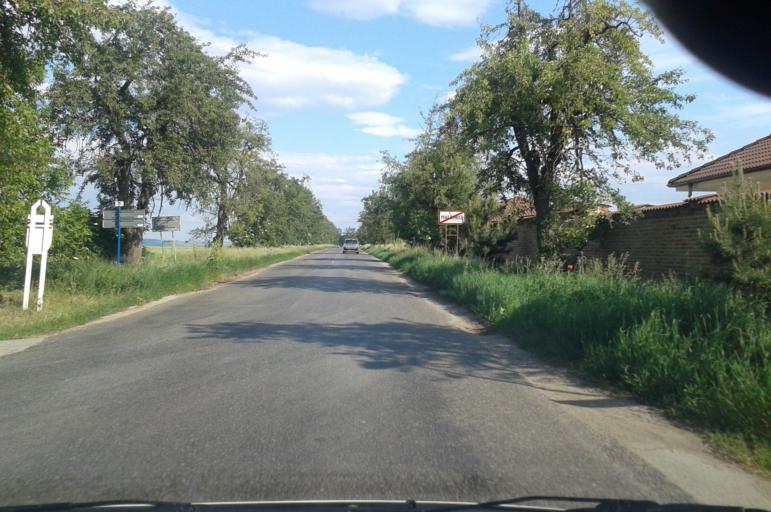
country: SK
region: Trnavsky
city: Leopoldov
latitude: 48.4495
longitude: 17.6809
